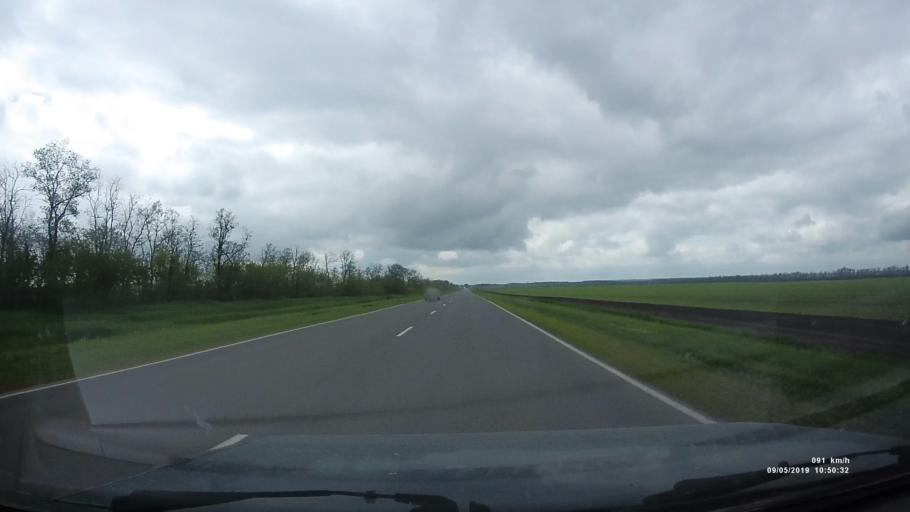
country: RU
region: Rostov
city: Peshkovo
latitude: 46.9274
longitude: 39.3555
